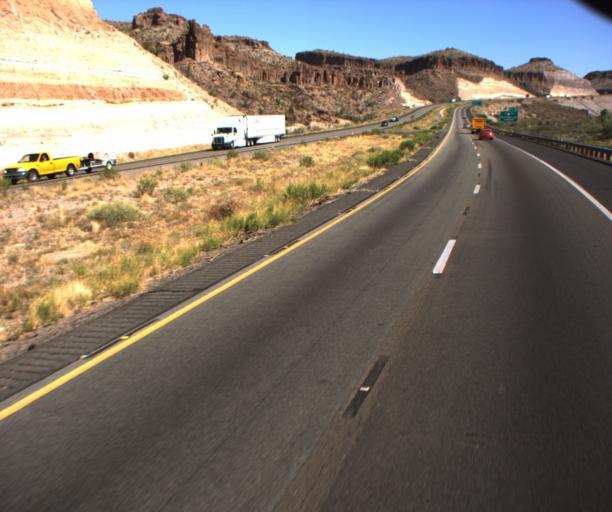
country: US
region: Arizona
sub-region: Mohave County
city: Kingman
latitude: 35.1659
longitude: -114.0738
